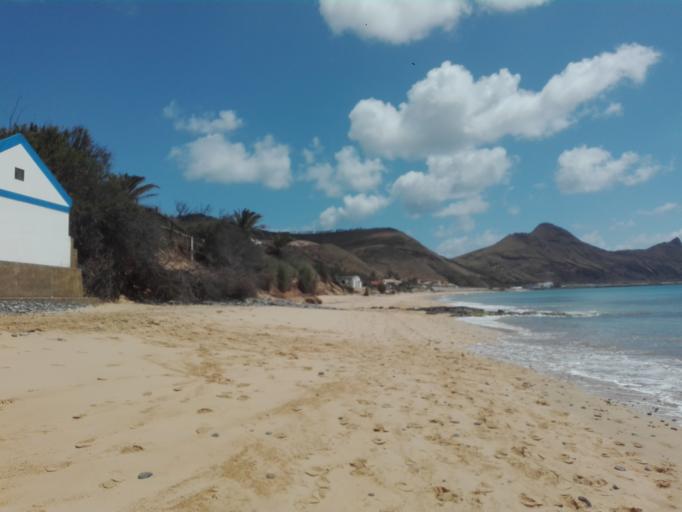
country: PT
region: Madeira
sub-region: Porto Santo
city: Vila de Porto Santo
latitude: 33.0602
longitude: -16.3298
